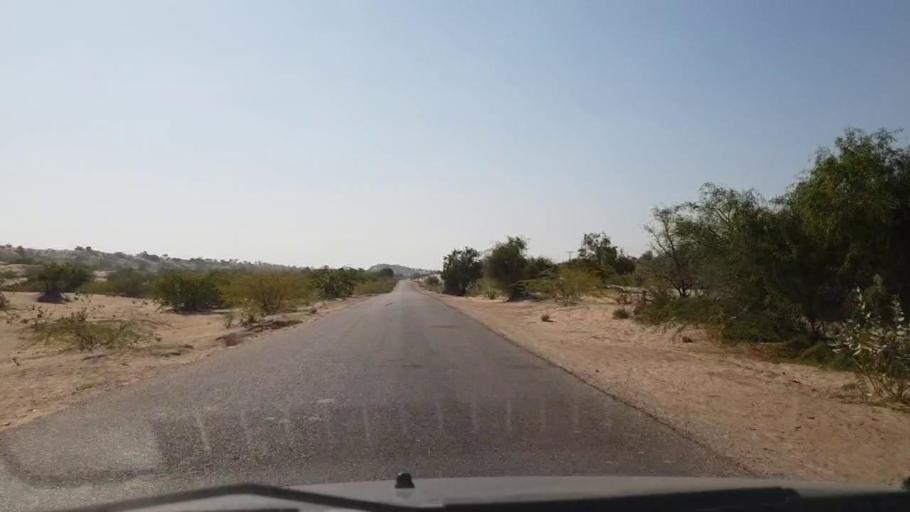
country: PK
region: Sindh
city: Diplo
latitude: 24.5662
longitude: 69.6770
